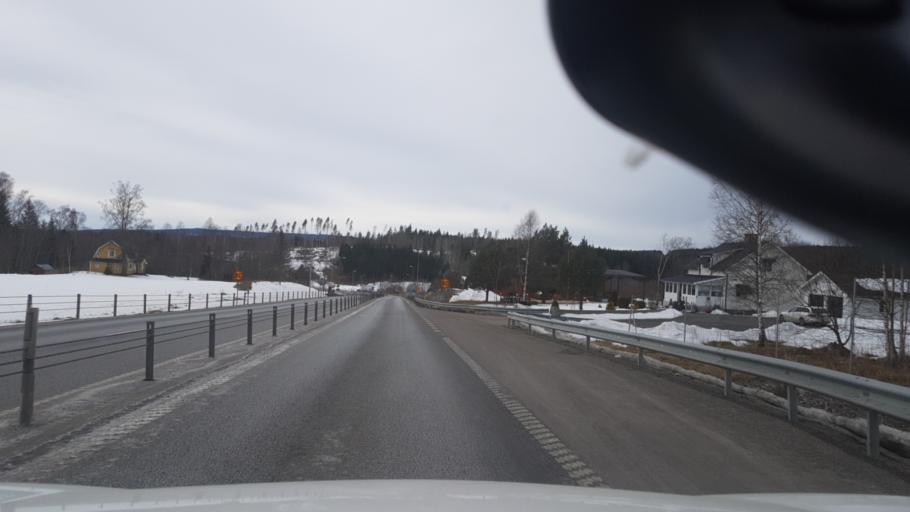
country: SE
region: Vaermland
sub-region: Eda Kommun
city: Amotfors
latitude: 59.7600
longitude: 12.4485
